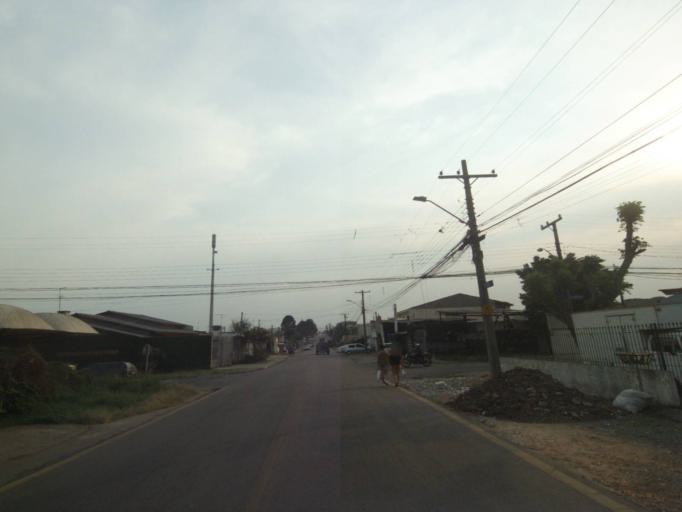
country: BR
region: Parana
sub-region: Sao Jose Dos Pinhais
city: Sao Jose dos Pinhais
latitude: -25.5264
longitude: -49.2699
